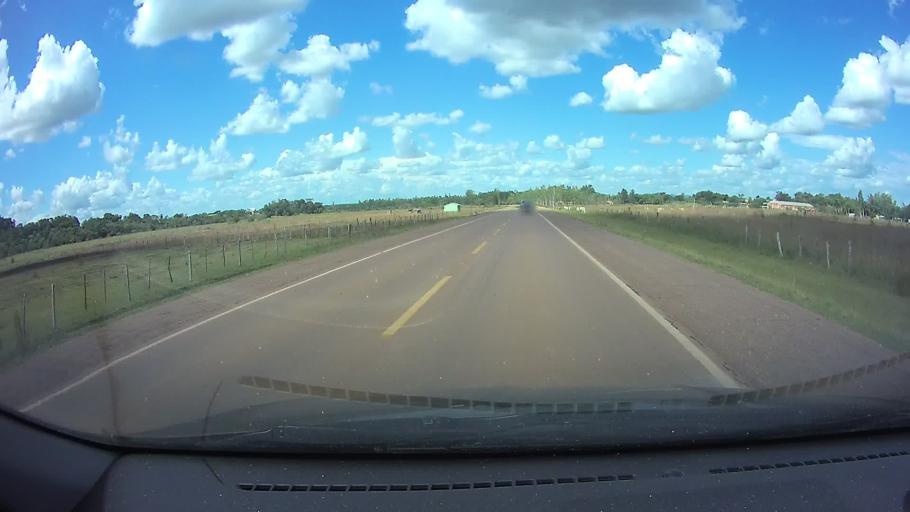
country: PY
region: Guaira
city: Itape
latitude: -25.9154
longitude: -56.6831
